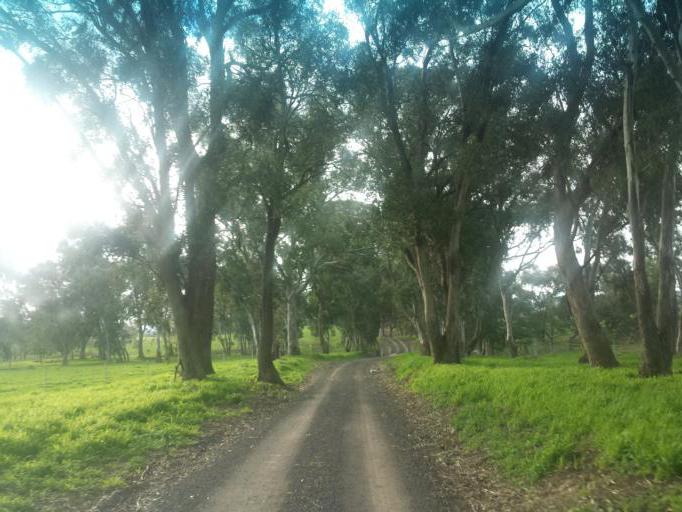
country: AU
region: Victoria
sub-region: Murrindindi
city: Kinglake West
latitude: -37.0391
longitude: 145.2502
